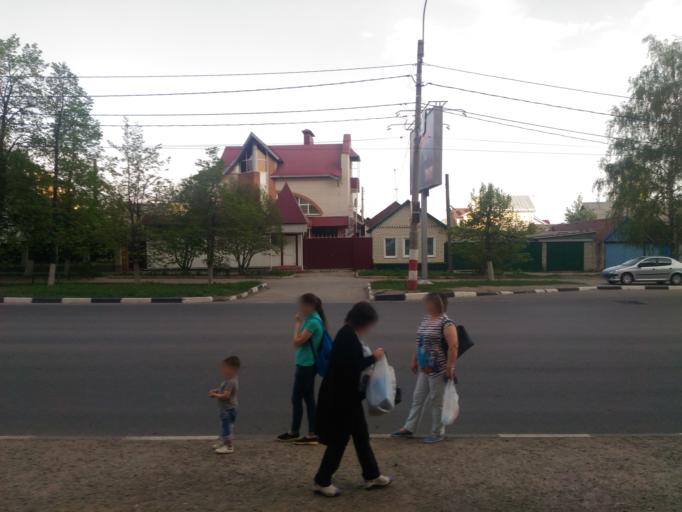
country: RU
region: Ulyanovsk
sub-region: Ulyanovskiy Rayon
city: Ulyanovsk
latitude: 54.3015
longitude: 48.3838
